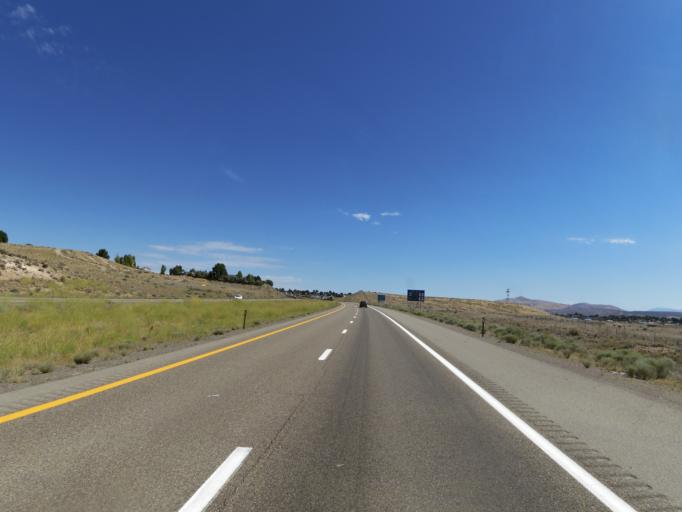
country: US
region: Nevada
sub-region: Elko County
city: Elko
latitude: 40.8258
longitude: -115.8027
